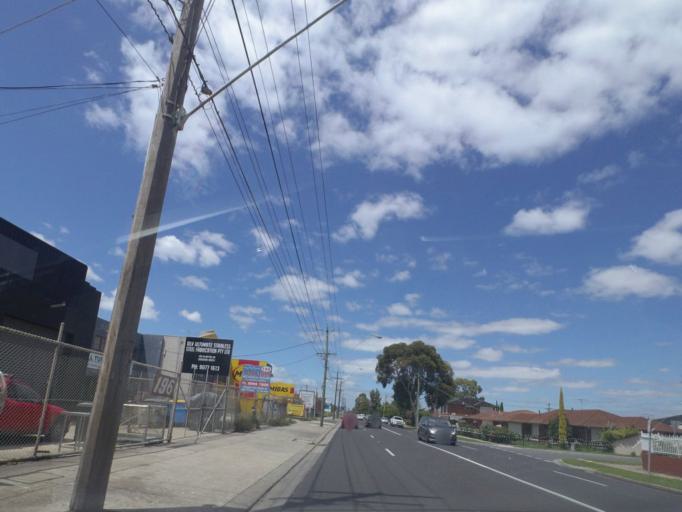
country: AU
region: Victoria
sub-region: Brimbank
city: Albion
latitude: -37.7562
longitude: 144.8326
